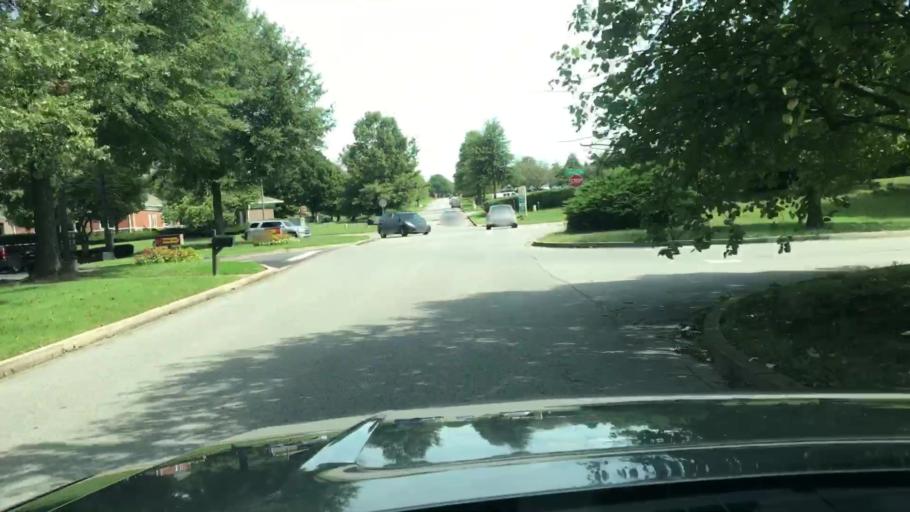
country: US
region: Tennessee
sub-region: Williamson County
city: Franklin
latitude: 35.9451
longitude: -86.8239
